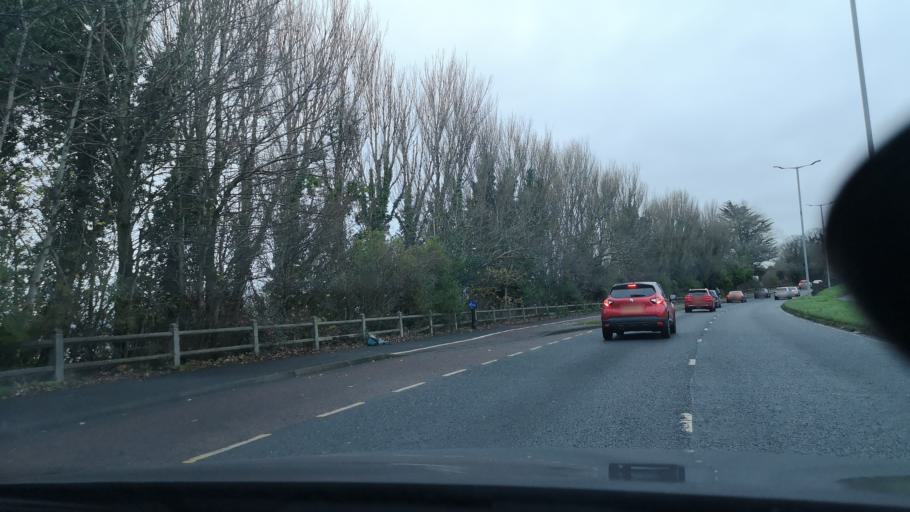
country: GB
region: Northern Ireland
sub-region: Castlereagh District
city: Castlereagh
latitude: 54.5798
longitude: -5.8713
